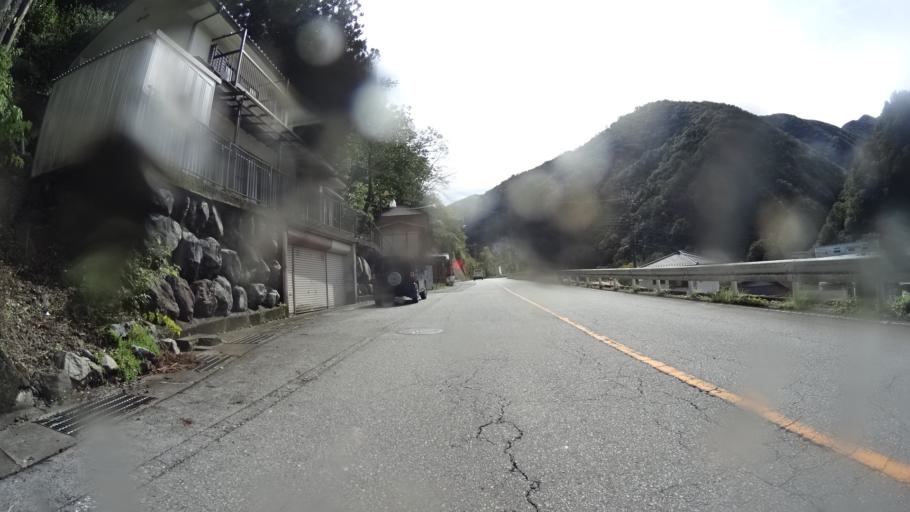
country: JP
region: Yamanashi
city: Otsuki
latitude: 35.7935
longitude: 138.9156
